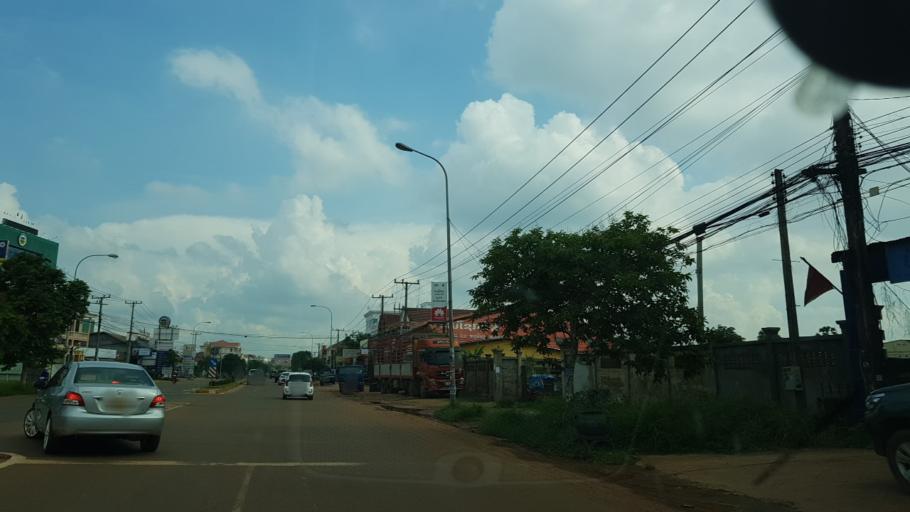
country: LA
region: Vientiane
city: Vientiane
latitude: 18.0267
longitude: 102.6517
